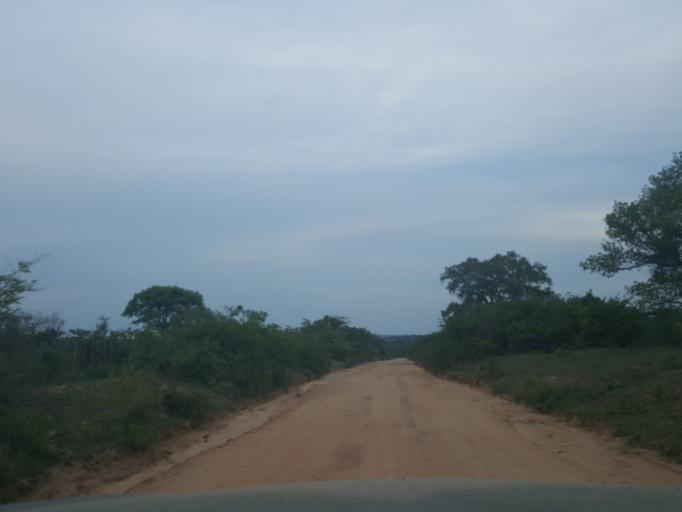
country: ZA
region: Limpopo
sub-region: Mopani District Municipality
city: Hoedspruit
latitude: -24.5804
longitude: 30.9908
